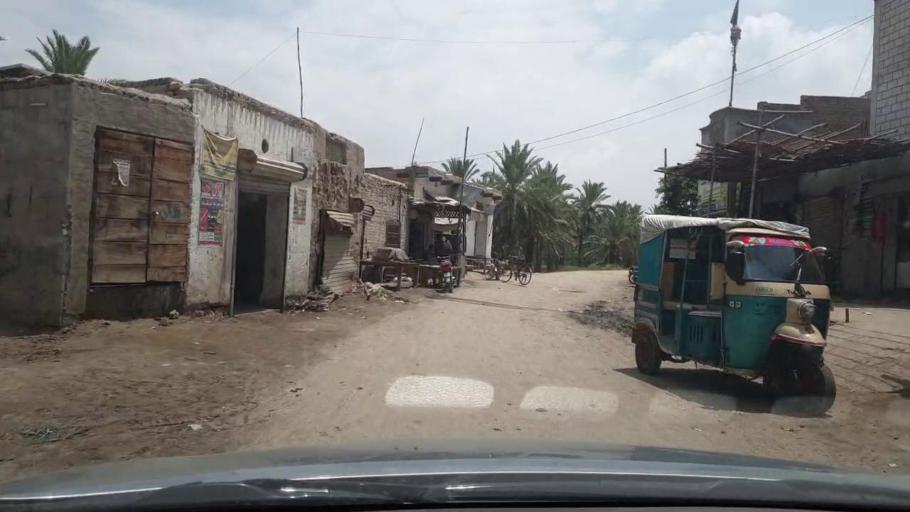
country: PK
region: Sindh
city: Khairpur
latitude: 27.4364
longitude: 68.7662
